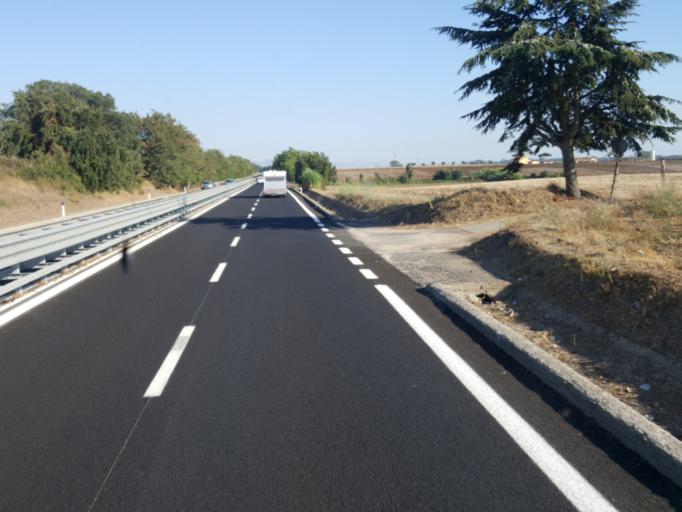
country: IT
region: Latium
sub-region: Provincia di Viterbo
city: Tarquinia
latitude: 42.2886
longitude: 11.6855
